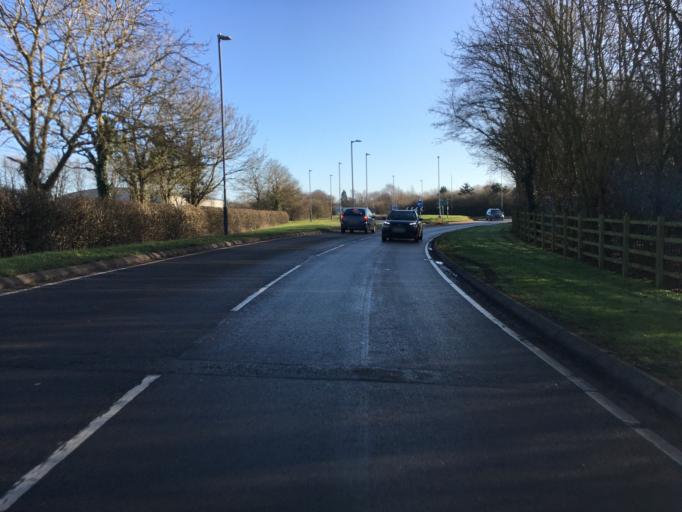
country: GB
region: England
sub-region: Warwickshire
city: Wellesbourne Mountford
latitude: 52.1964
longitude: -1.6065
